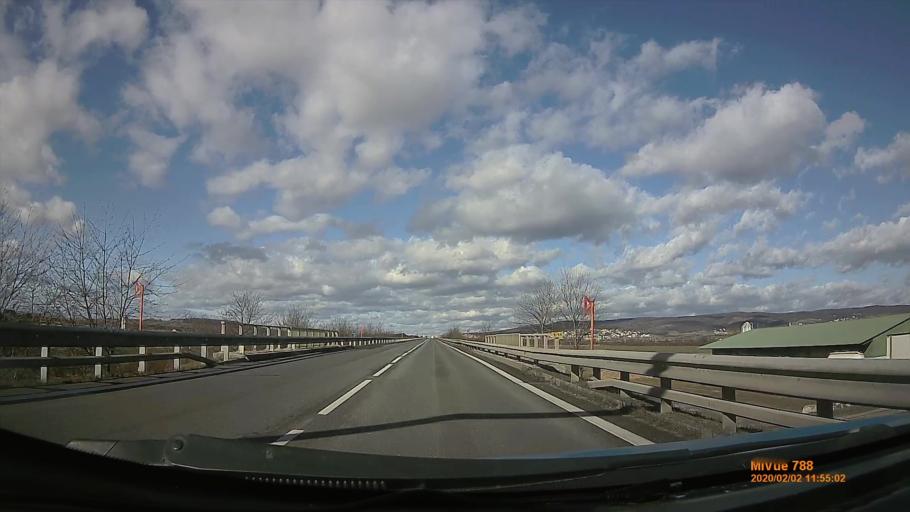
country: AT
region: Burgenland
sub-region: Eisenstadt-Umgebung
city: Wulkaprodersdorf
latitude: 47.8011
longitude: 16.5118
